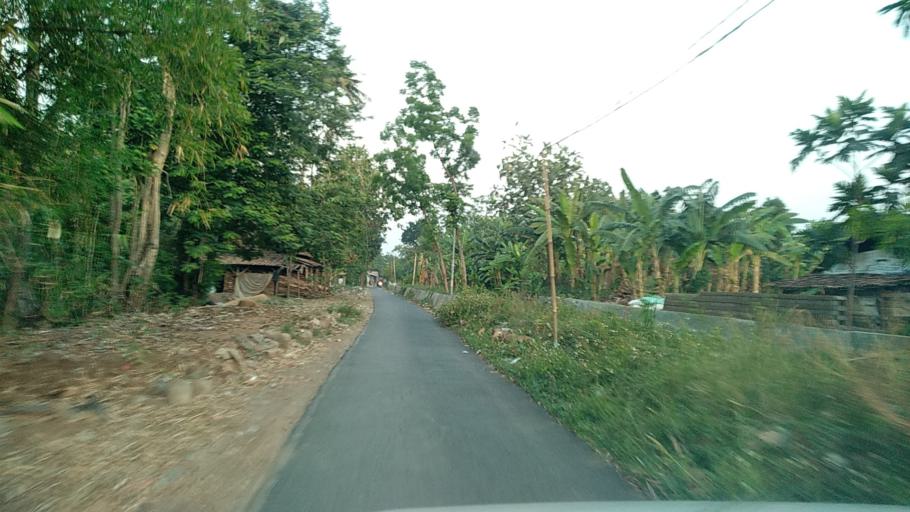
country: ID
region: Central Java
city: Semarang
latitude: -6.9715
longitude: 110.3102
